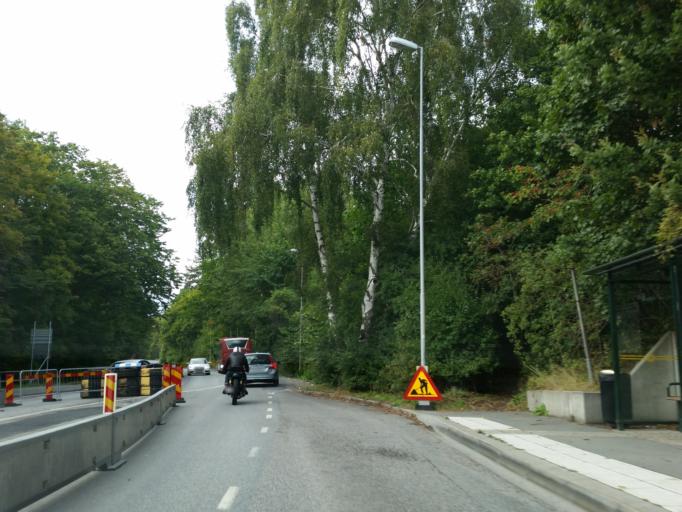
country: SE
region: Stockholm
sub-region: Sollentuna Kommun
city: Sollentuna
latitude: 59.4420
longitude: 17.9494
